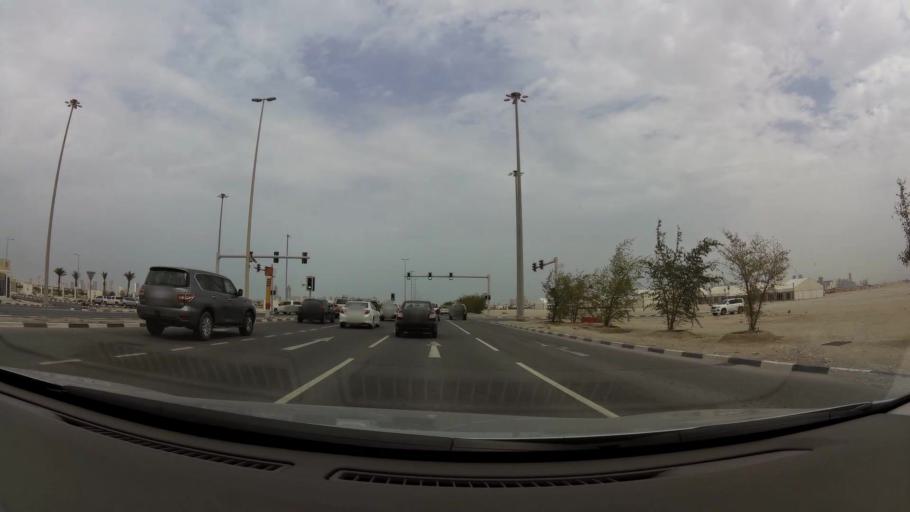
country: QA
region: Baladiyat ad Dawhah
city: Doha
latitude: 25.3579
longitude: 51.4876
